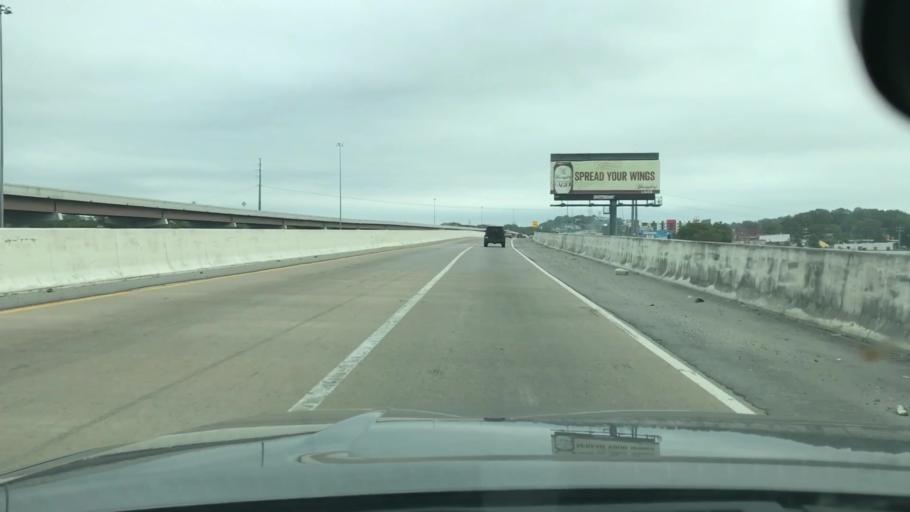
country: US
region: Tennessee
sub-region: Davidson County
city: Belle Meade
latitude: 36.1529
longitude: -86.8536
